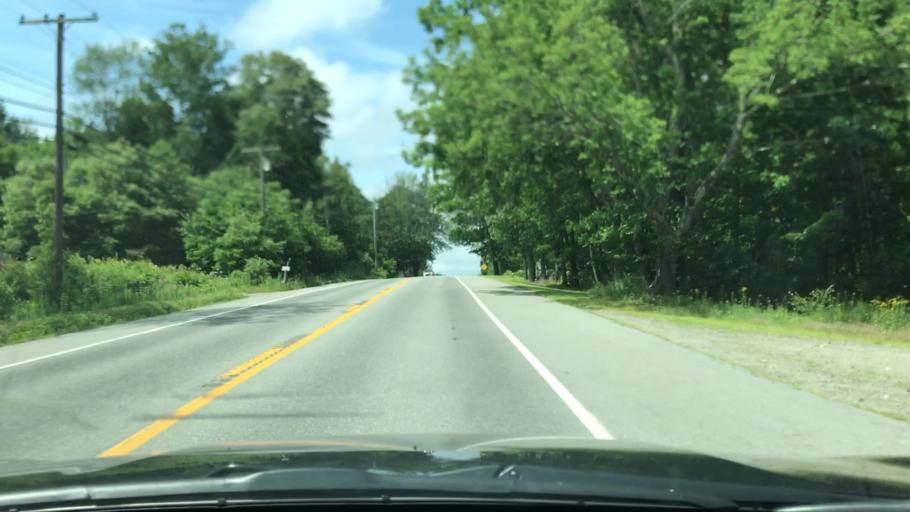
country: US
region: Maine
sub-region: Waldo County
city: Belfast
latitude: 44.3872
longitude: -68.9888
